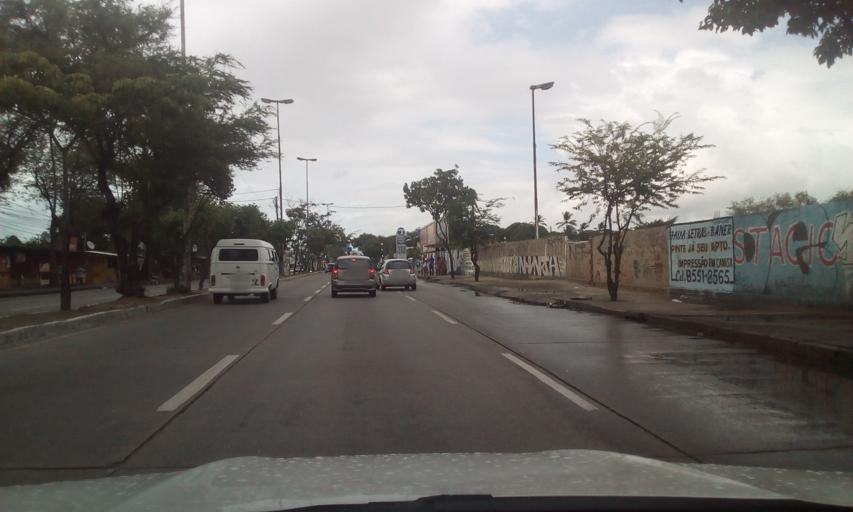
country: BR
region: Pernambuco
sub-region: Recife
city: Recife
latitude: -8.0990
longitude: -34.9284
